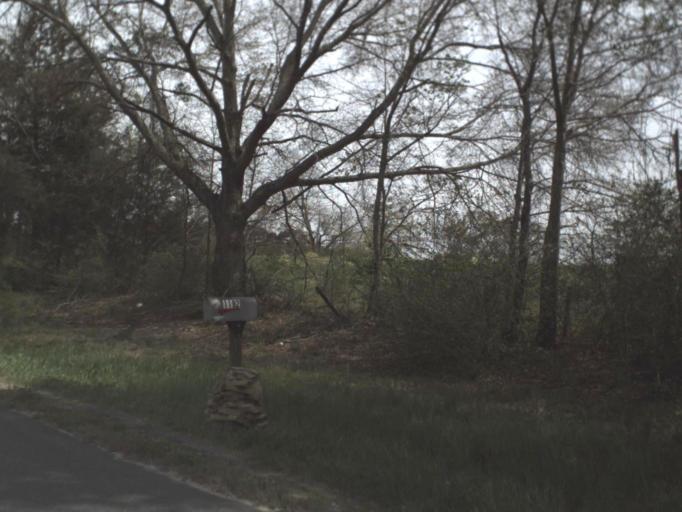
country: US
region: Florida
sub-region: Jackson County
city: Graceville
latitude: 30.9627
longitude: -85.5596
